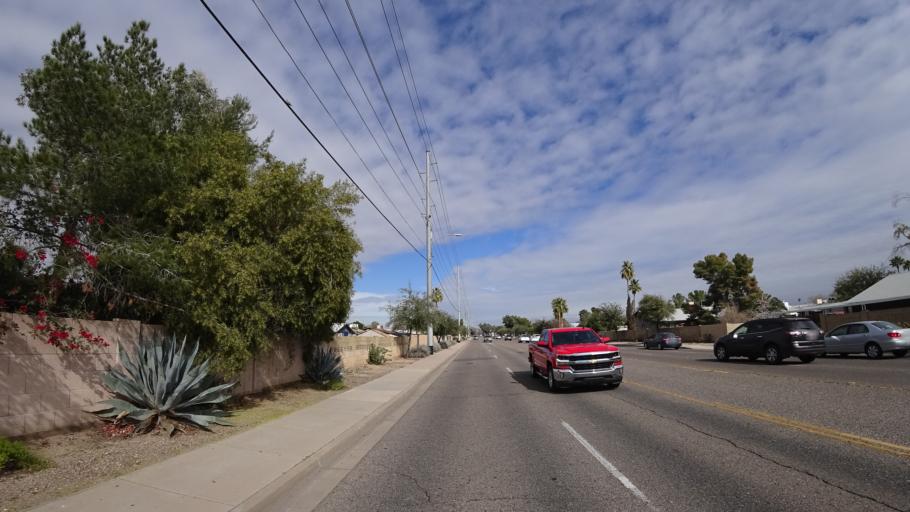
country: US
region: Arizona
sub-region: Maricopa County
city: Peoria
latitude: 33.6292
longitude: -112.1858
